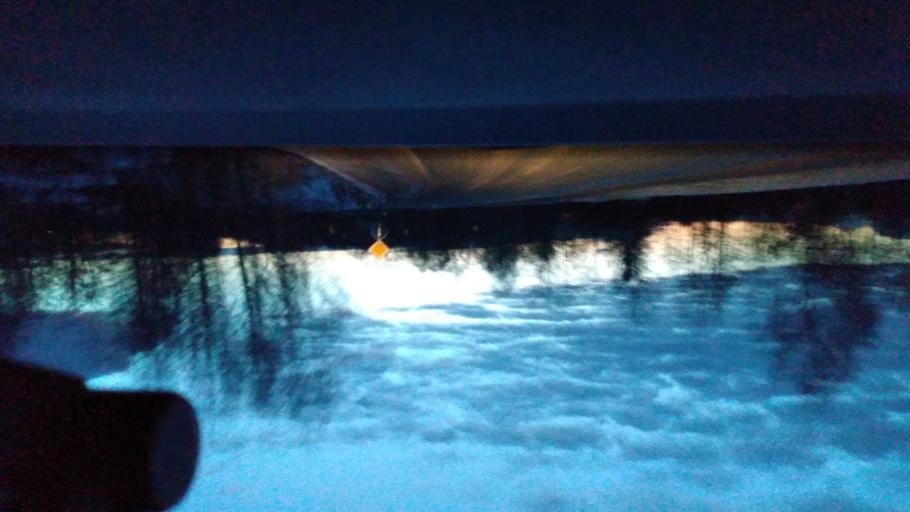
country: RU
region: Moskovskaya
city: Krasnaya Poyma
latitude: 55.1367
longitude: 39.2052
